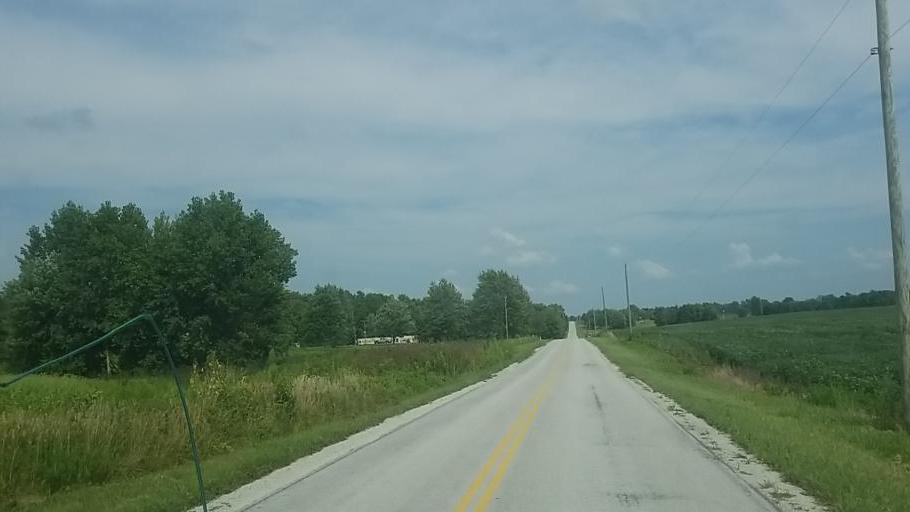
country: US
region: Ohio
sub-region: Hardin County
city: Forest
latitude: 40.8038
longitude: -83.5511
